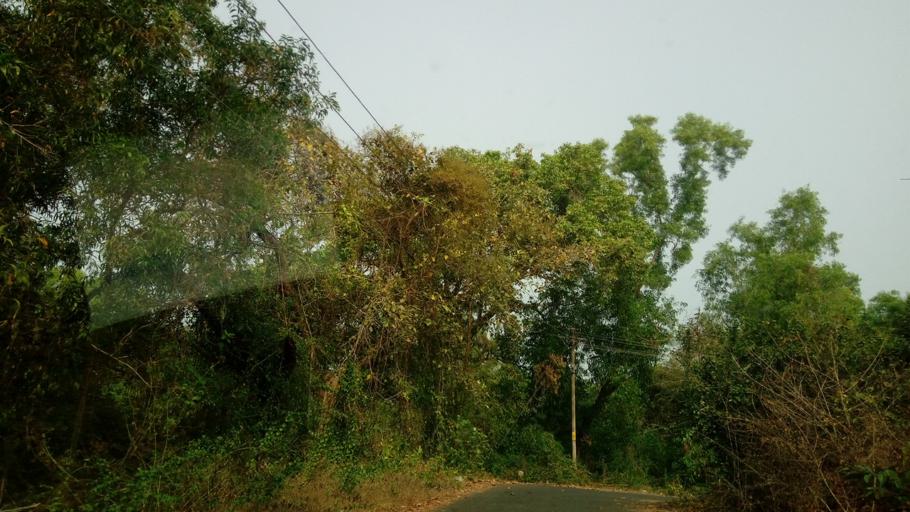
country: IN
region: Goa
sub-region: South Goa
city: Varca
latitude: 15.2190
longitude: 73.9344
